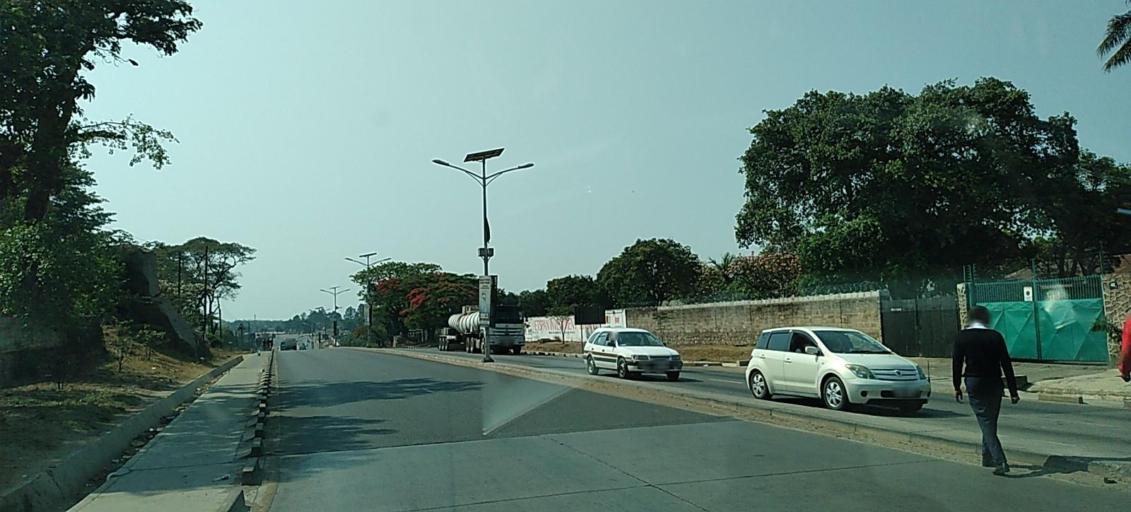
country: ZM
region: Copperbelt
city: Chingola
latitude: -12.5529
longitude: 27.8697
